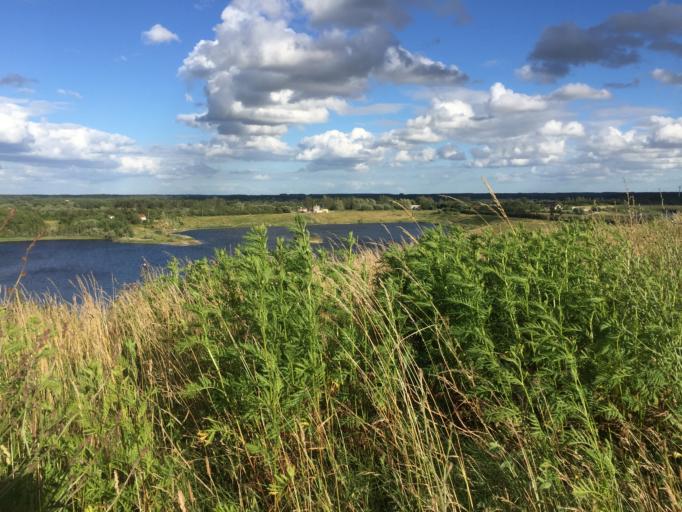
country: DK
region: South Denmark
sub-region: Kerteminde Kommune
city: Langeskov
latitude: 55.3336
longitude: 10.5342
